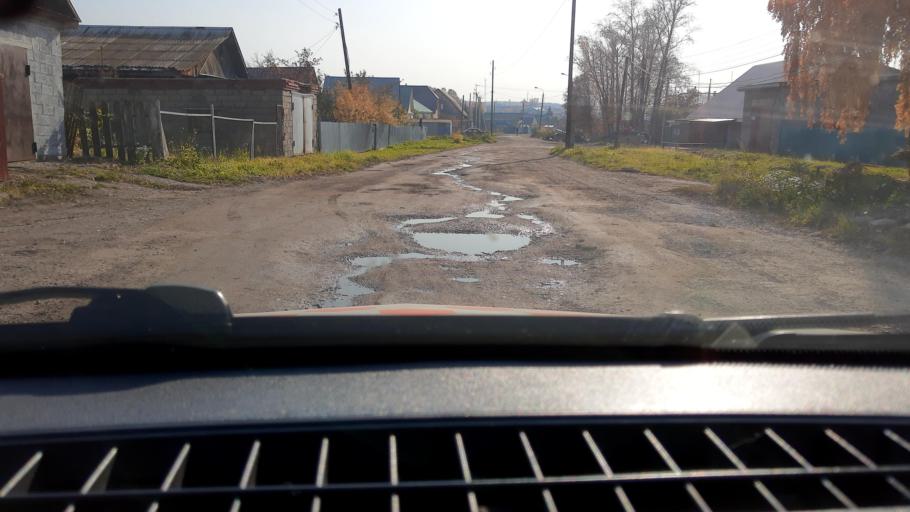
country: RU
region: Bashkortostan
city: Ufa
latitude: 54.8427
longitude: 56.1550
